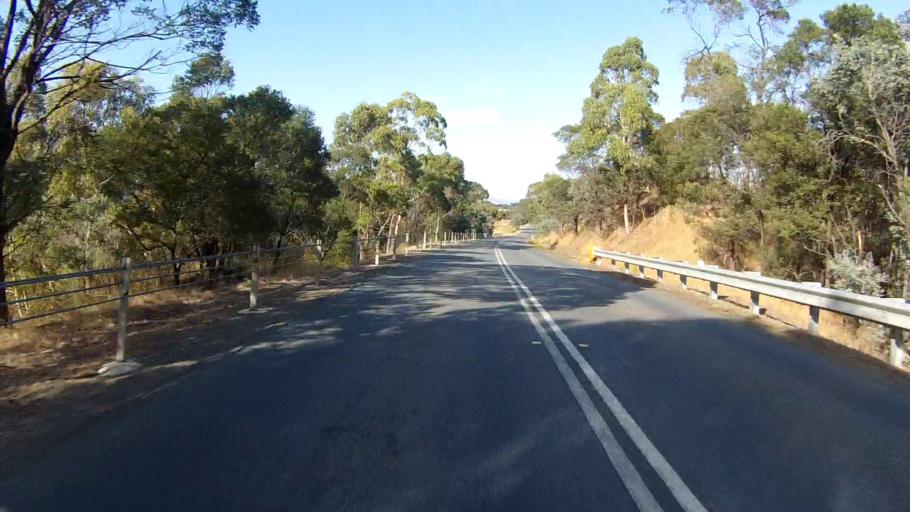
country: AU
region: Tasmania
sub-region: Derwent Valley
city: New Norfolk
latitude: -42.7588
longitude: 147.1393
